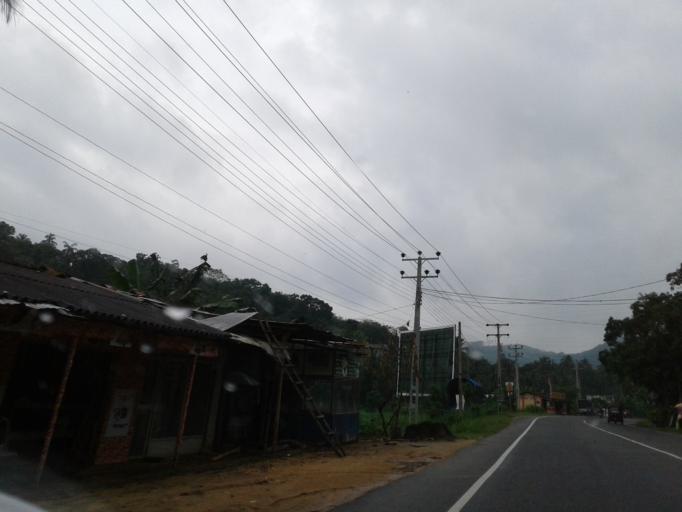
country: LK
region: Western
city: Gampaha
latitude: 7.2379
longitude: 80.2278
